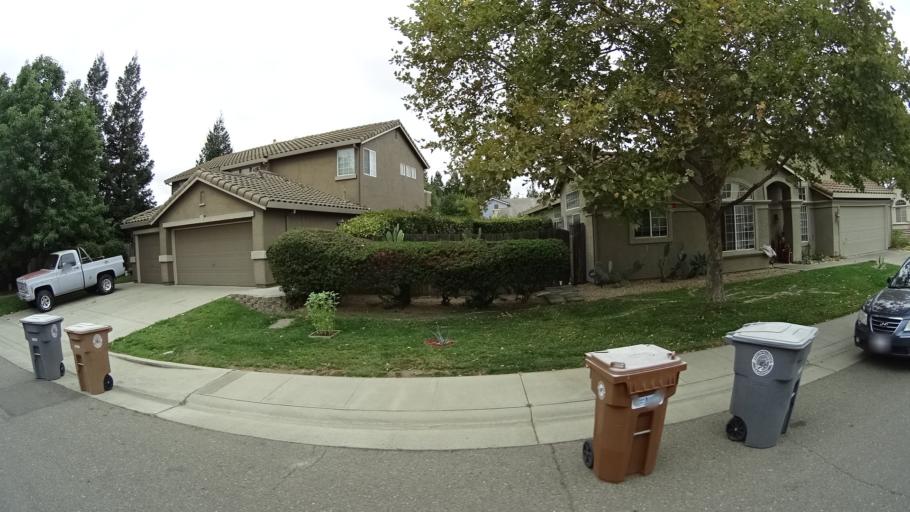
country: US
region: California
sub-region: Sacramento County
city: Laguna
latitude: 38.4184
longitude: -121.4539
